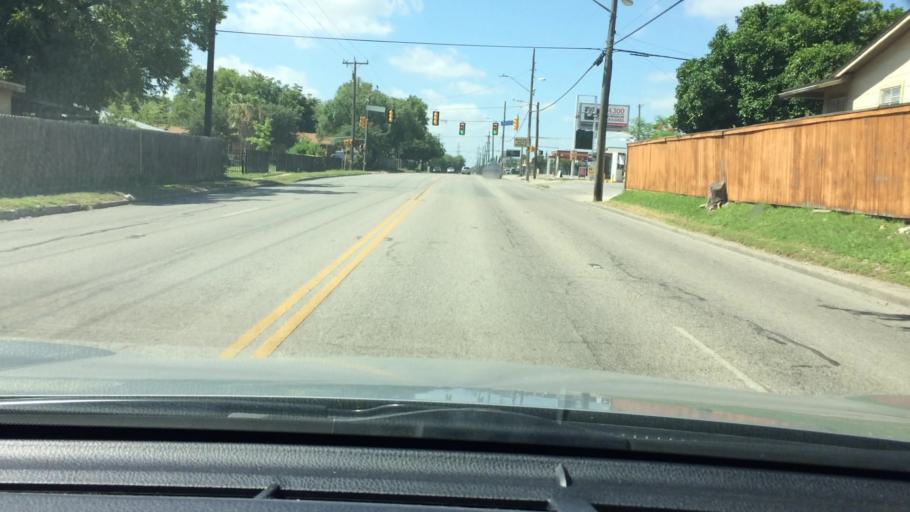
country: US
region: Texas
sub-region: Bexar County
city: Balcones Heights
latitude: 29.5000
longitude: -98.5351
